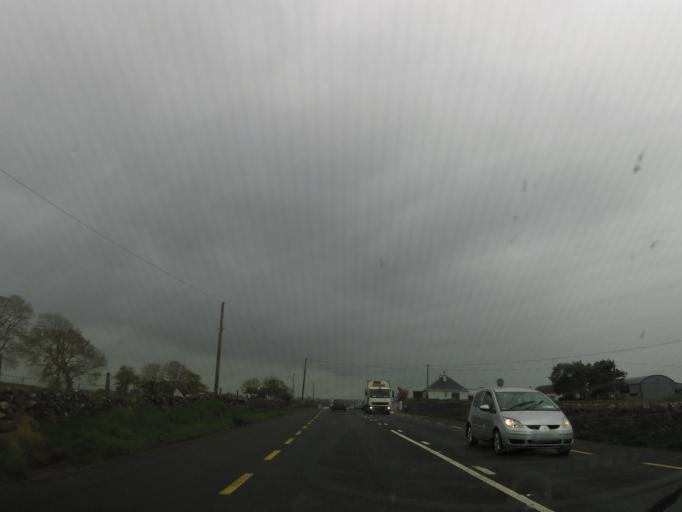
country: IE
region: Connaught
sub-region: County Galway
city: Tuam
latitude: 53.4987
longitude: -8.8886
